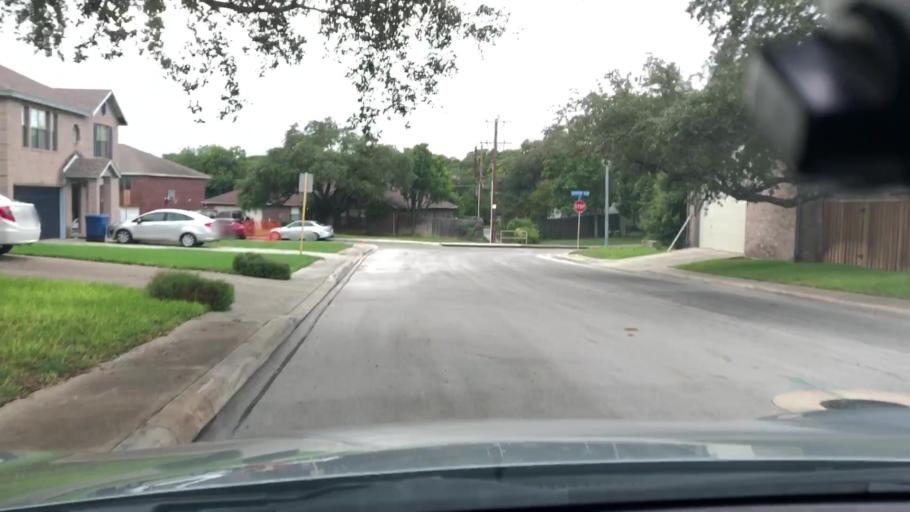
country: US
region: Texas
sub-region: Bexar County
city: Leon Valley
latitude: 29.5062
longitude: -98.6758
